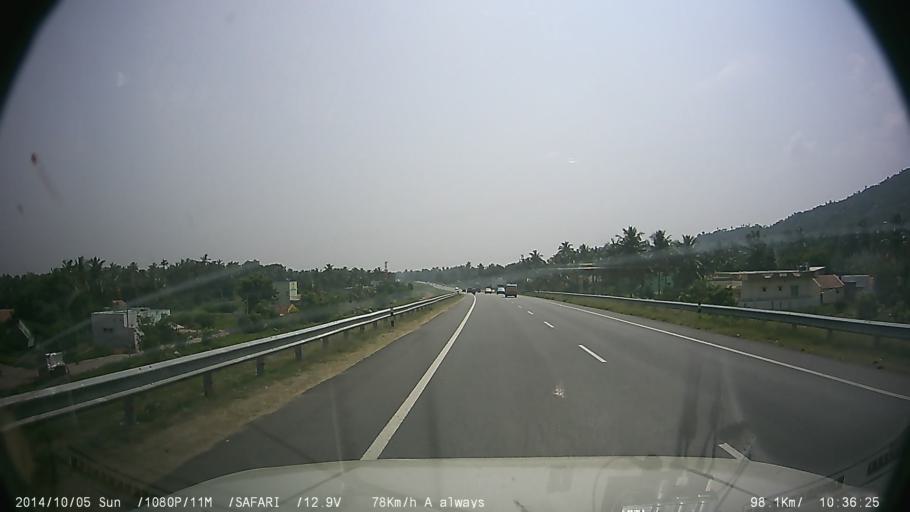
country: IN
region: Tamil Nadu
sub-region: Salem
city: Salem
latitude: 11.6605
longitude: 78.2152
